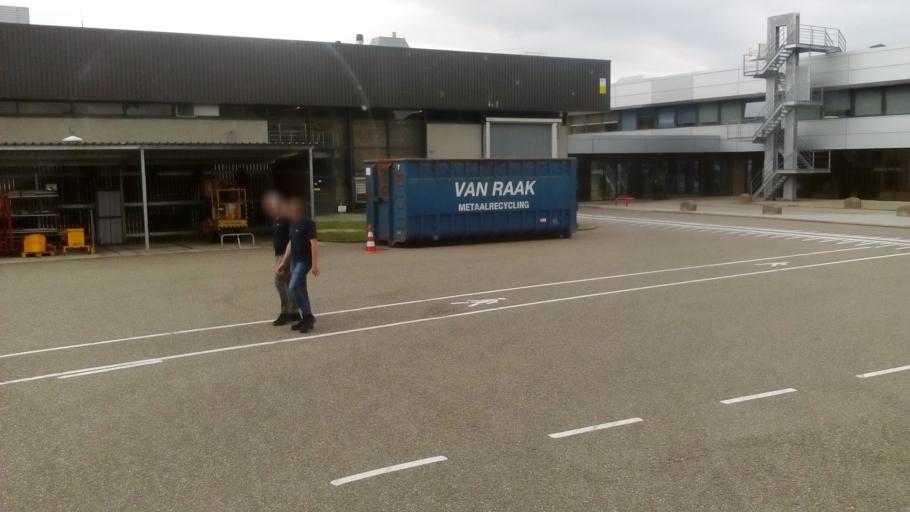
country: NL
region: North Brabant
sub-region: Gemeente Goirle
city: Goirle
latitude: 51.5411
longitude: 5.0537
